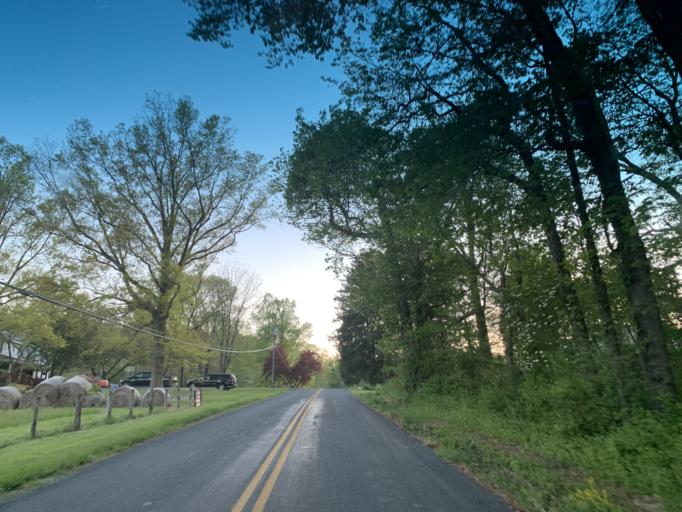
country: US
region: Maryland
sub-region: Harford County
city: Riverside
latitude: 39.5287
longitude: -76.2320
